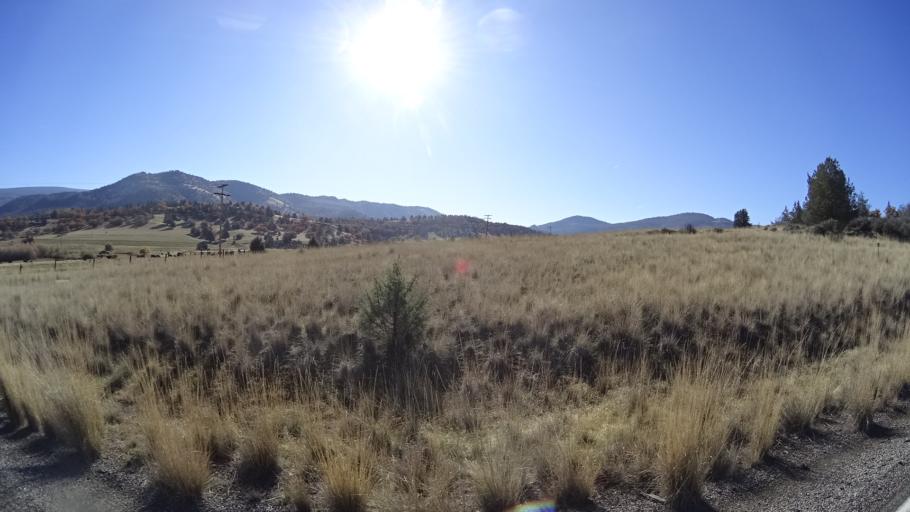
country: US
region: California
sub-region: Siskiyou County
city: Montague
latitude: 41.9040
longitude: -122.3838
